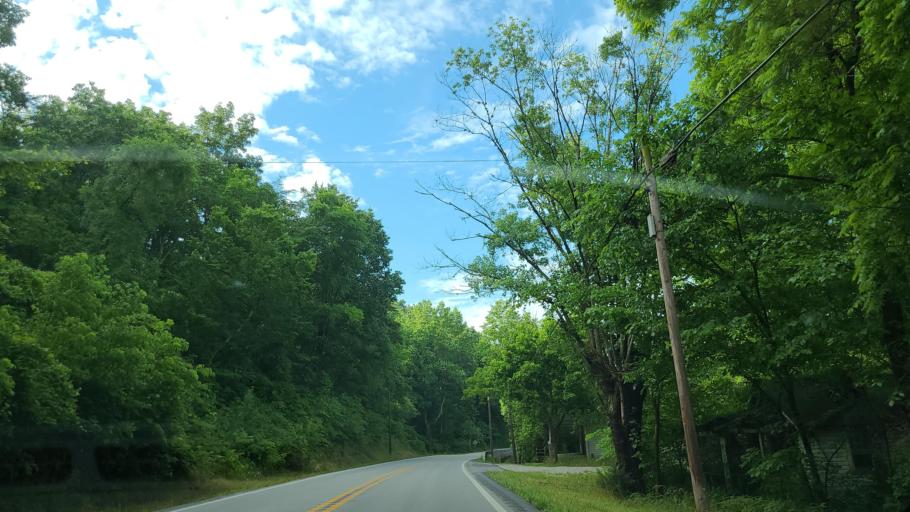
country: US
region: Kentucky
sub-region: Whitley County
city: Williamsburg
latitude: 36.7345
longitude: -84.1300
